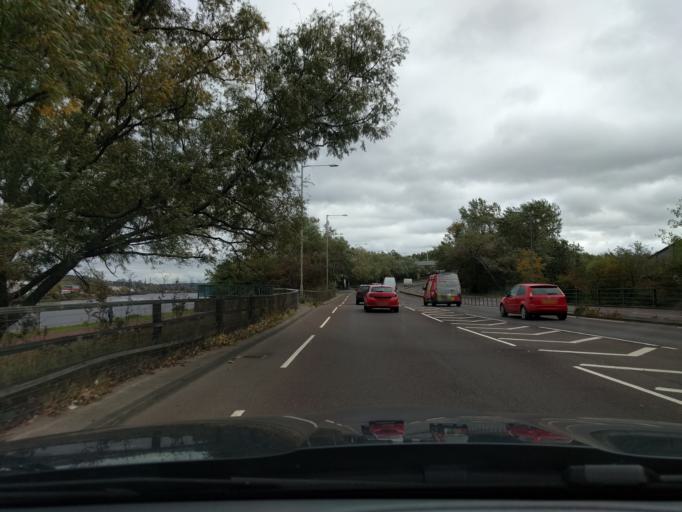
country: GB
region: England
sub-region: Newcastle upon Tyne
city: Benwell
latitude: 54.9655
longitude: -1.6888
